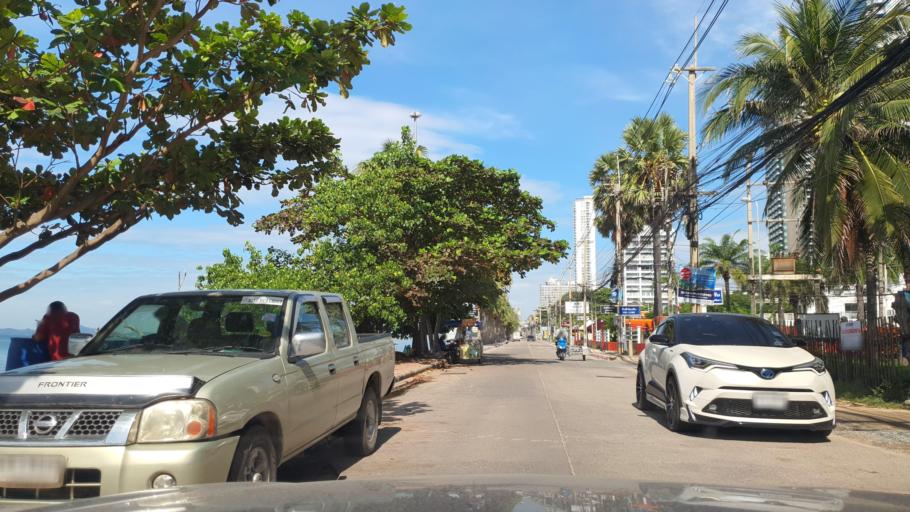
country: TH
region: Chon Buri
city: Phatthaya
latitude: 12.8681
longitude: 100.8914
